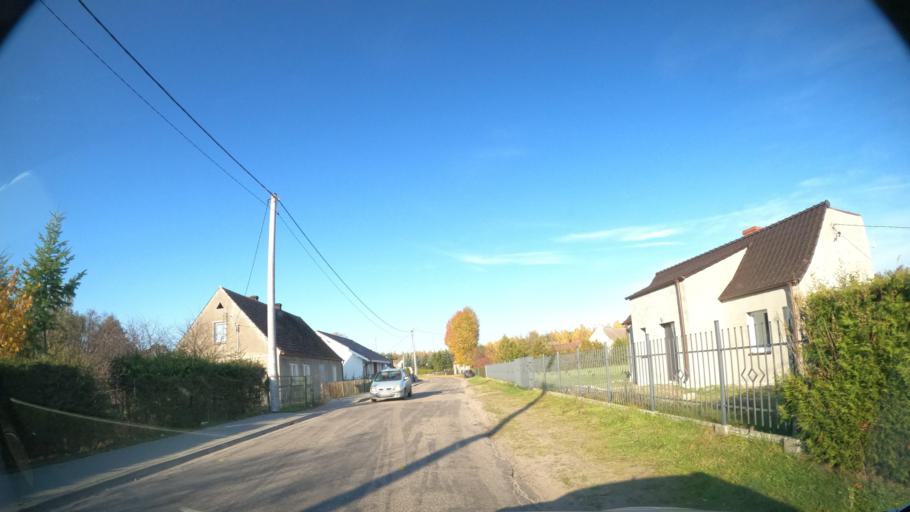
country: PL
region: Greater Poland Voivodeship
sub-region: Powiat zlotowski
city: Sypniewo
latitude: 53.3515
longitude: 16.5727
